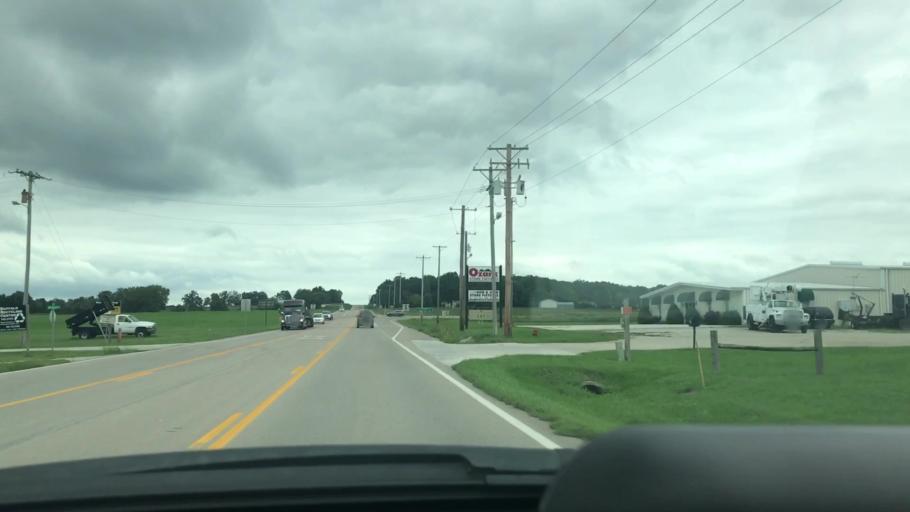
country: US
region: Missouri
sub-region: Dallas County
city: Buffalo
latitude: 37.6657
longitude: -93.1034
